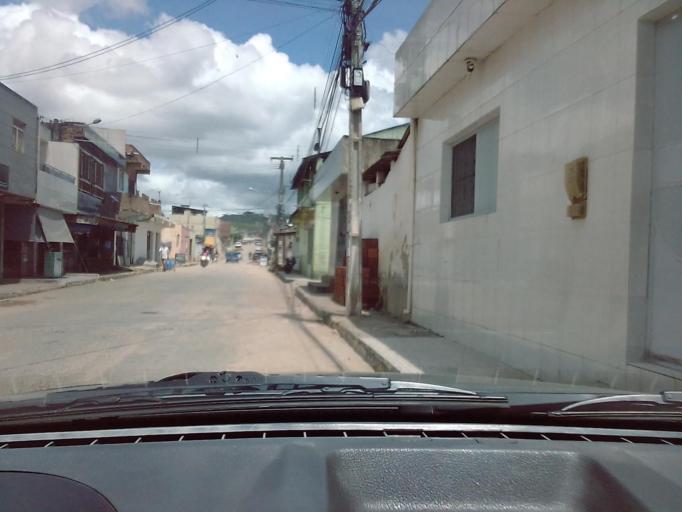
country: BR
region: Pernambuco
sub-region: Vitoria De Santo Antao
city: Vitoria de Santo Antao
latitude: -8.1256
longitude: -35.2939
